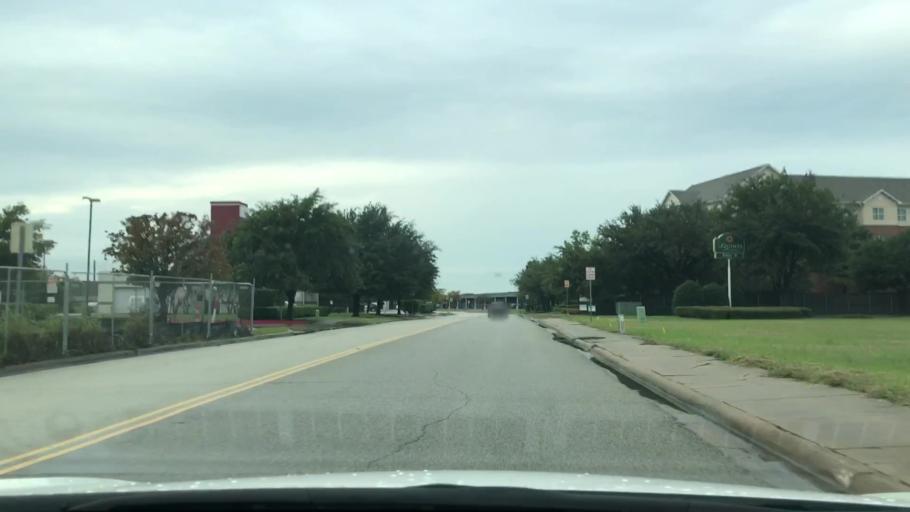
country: US
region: Texas
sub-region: Dallas County
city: Coppell
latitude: 32.9165
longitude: -97.0160
